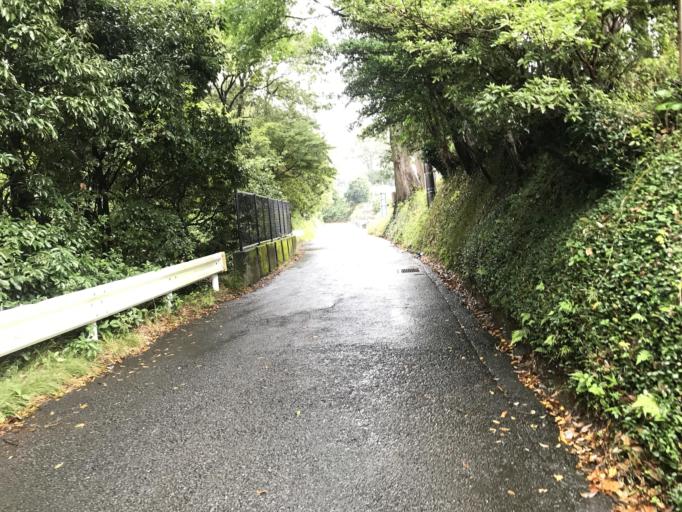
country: JP
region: Kanagawa
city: Zama
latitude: 35.5493
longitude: 139.3250
